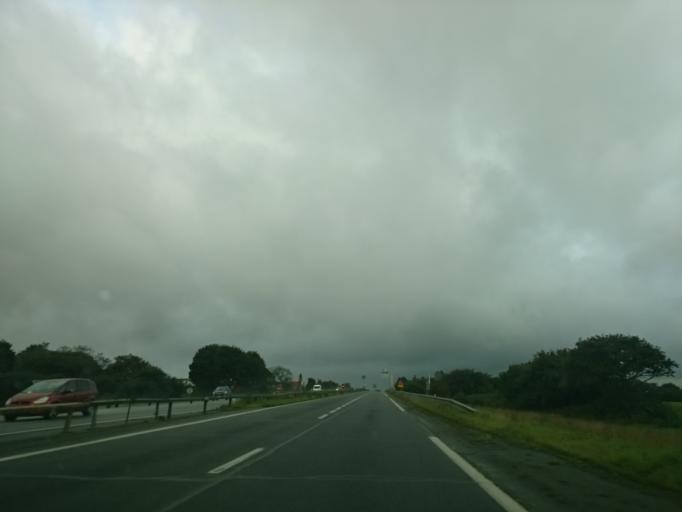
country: FR
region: Brittany
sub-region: Departement du Finistere
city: Gouesnou
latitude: 48.4341
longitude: -4.4397
